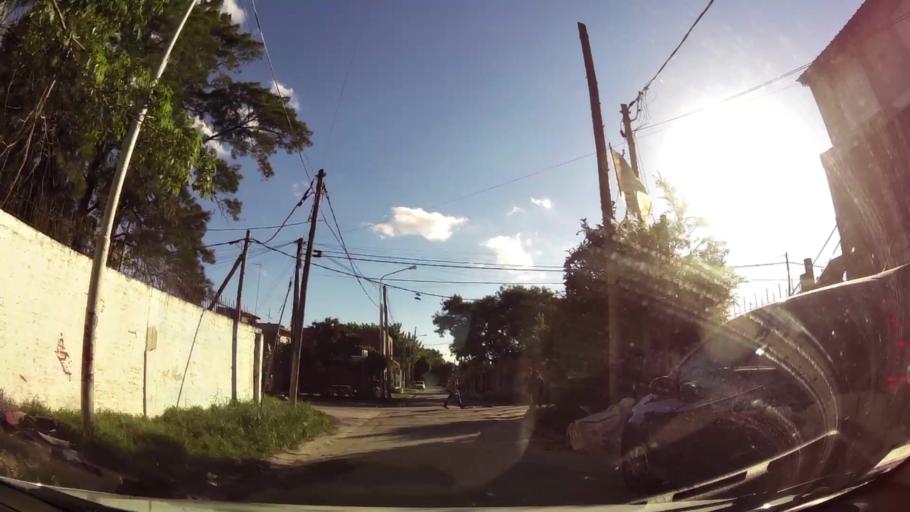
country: AR
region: Buenos Aires
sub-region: Partido de Moron
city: Moron
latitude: -34.6805
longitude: -58.6206
